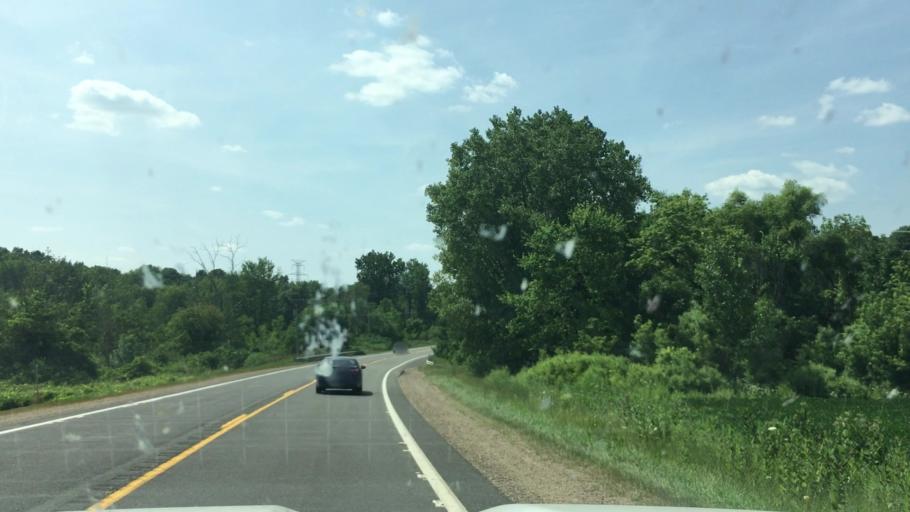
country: US
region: Michigan
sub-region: Allegan County
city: Plainwell
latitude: 42.4368
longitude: -85.5783
